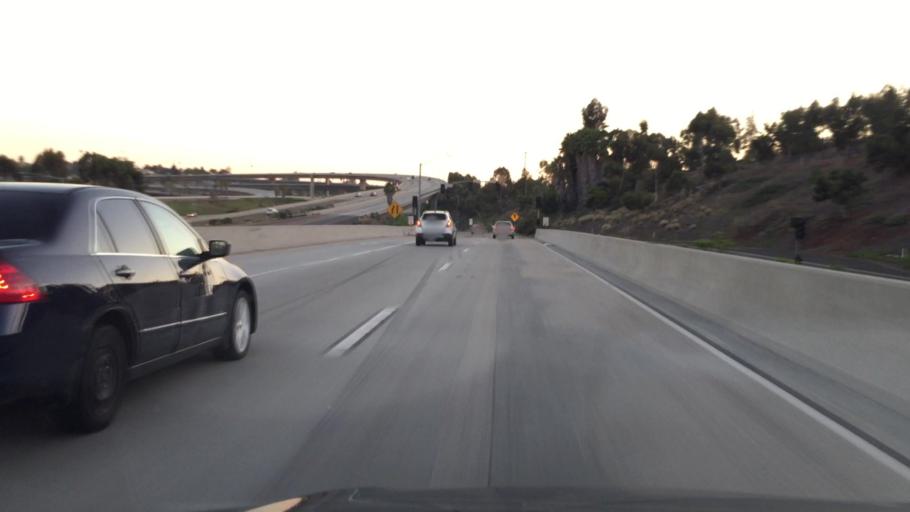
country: US
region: California
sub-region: San Diego County
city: Spring Valley
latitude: 32.7522
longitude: -117.0144
